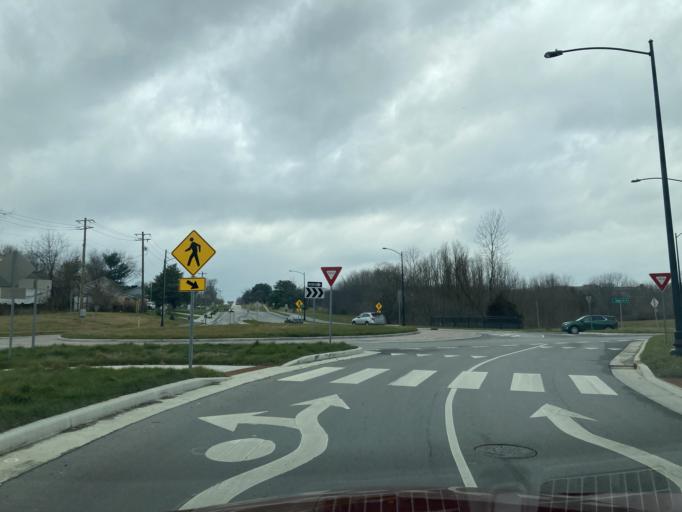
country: US
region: Indiana
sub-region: Monroe County
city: Bloomington
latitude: 39.1216
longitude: -86.5387
